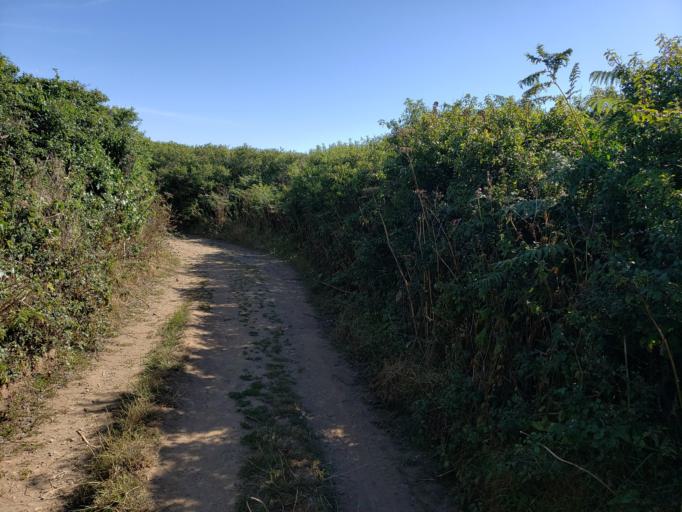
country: GB
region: England
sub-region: Cornwall
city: St Ives
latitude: 50.2110
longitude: -5.5016
